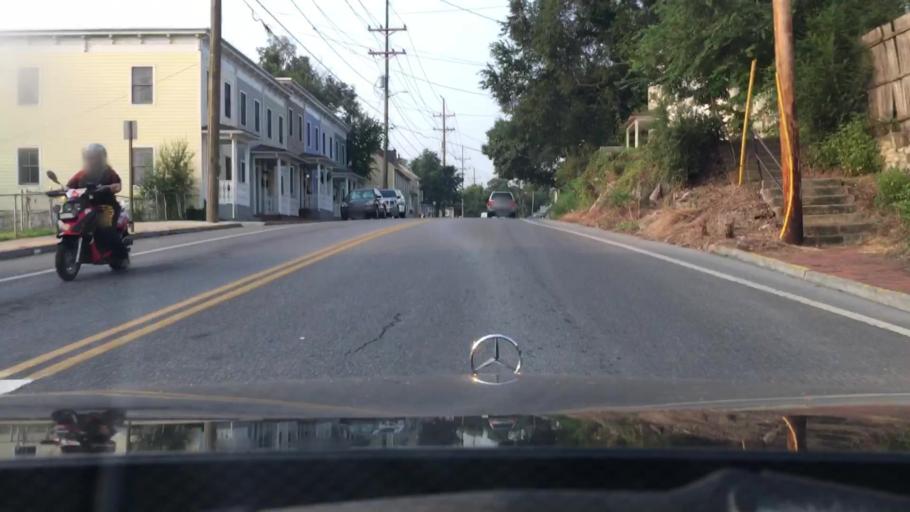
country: US
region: Virginia
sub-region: City of Winchester
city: Winchester
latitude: 39.1813
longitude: -78.1635
